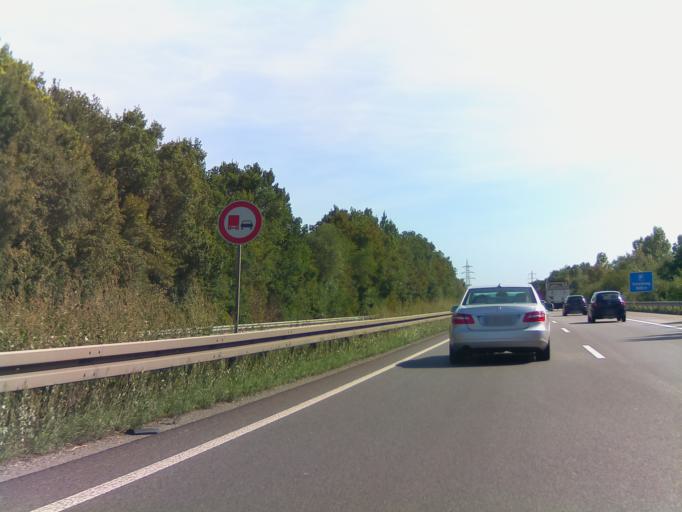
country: DE
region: Hesse
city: Zwingenberg
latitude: 49.7108
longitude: 8.5975
